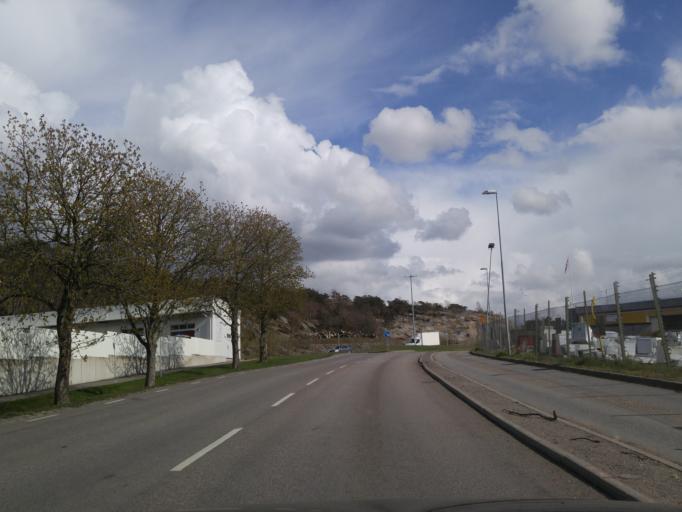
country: SE
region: Vaestra Goetaland
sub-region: Goteborg
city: Majorna
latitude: 57.6581
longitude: 11.9469
